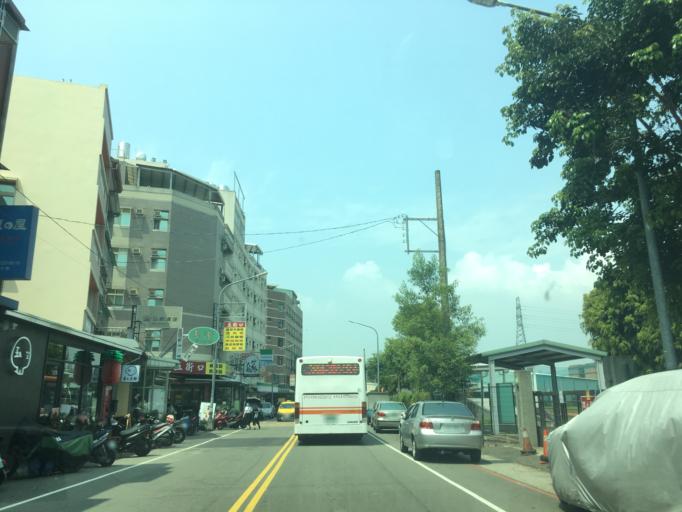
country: TW
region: Taiwan
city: Zhongxing New Village
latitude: 24.0440
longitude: 120.6886
